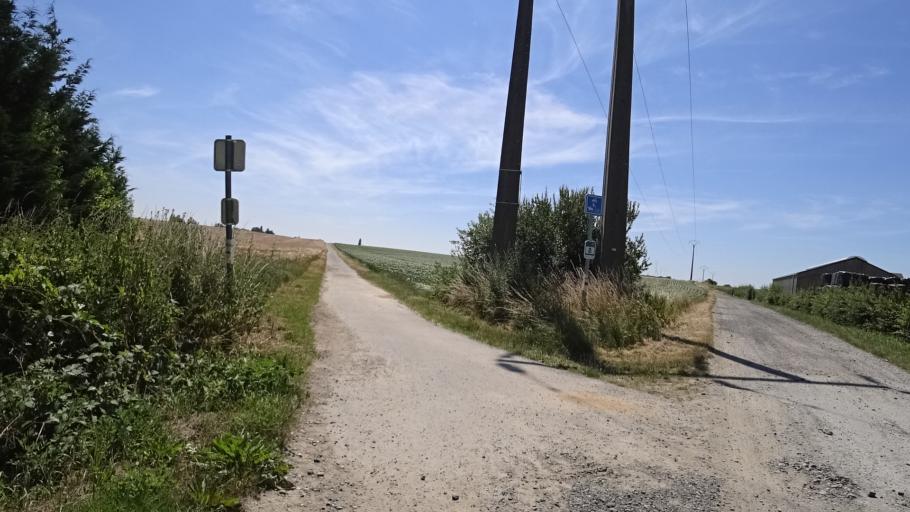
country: BE
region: Wallonia
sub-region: Province de Namur
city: Gembloux
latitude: 50.5750
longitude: 4.6793
